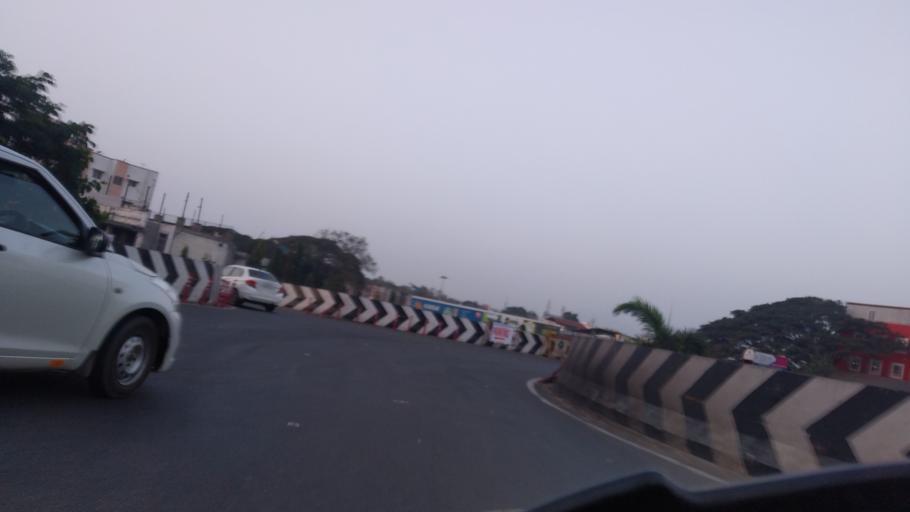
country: IN
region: Tamil Nadu
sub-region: Coimbatore
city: Coimbatore
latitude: 11.0015
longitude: 76.9630
